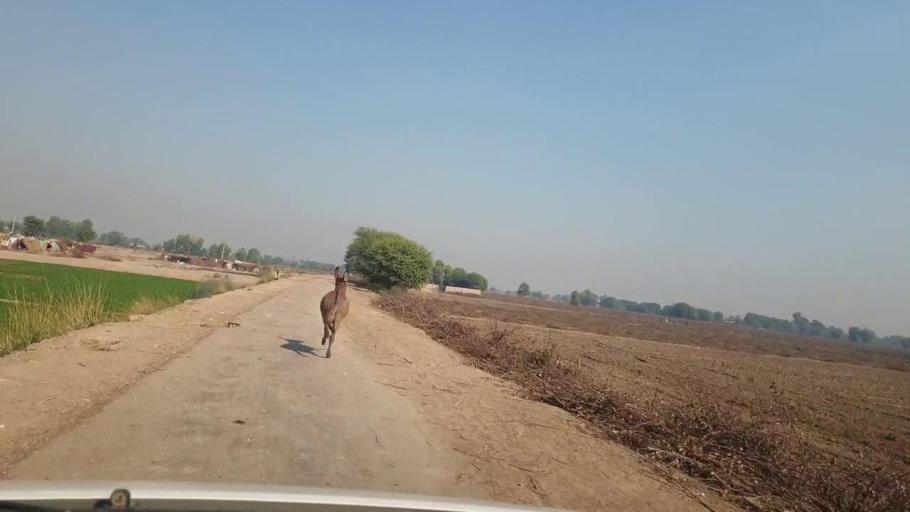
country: PK
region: Sindh
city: Bhan
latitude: 26.6138
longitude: 67.7605
